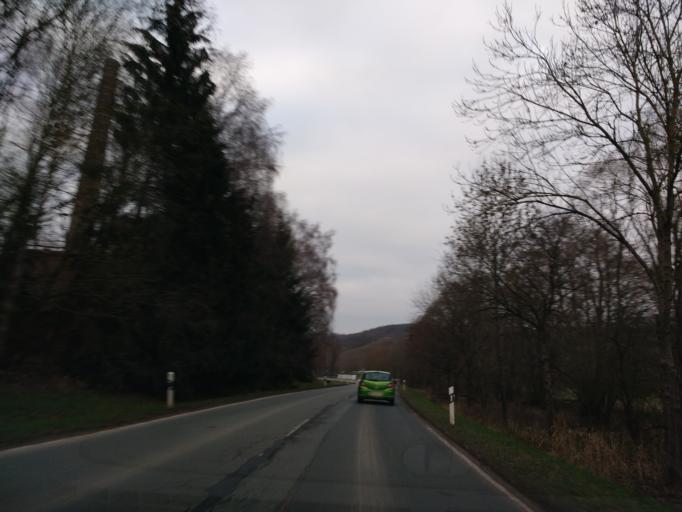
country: DE
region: Hesse
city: Bebra
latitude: 51.0141
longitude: 9.7742
